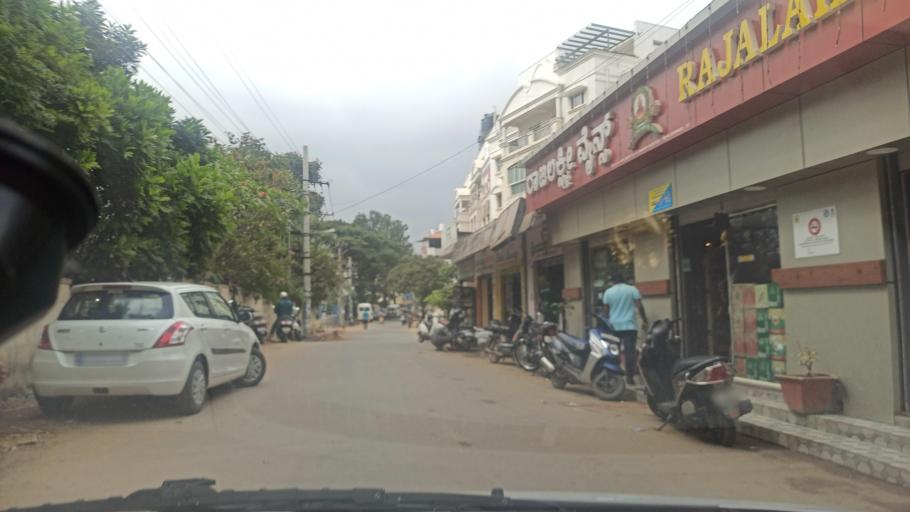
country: IN
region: Karnataka
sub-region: Bangalore Urban
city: Yelahanka
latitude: 13.0368
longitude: 77.5938
